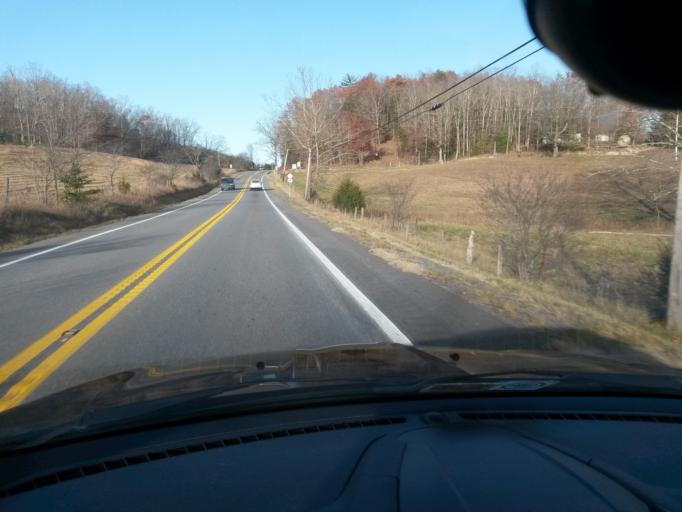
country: US
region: Virginia
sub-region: Alleghany County
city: Clifton Forge
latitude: 37.7328
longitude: -79.8005
